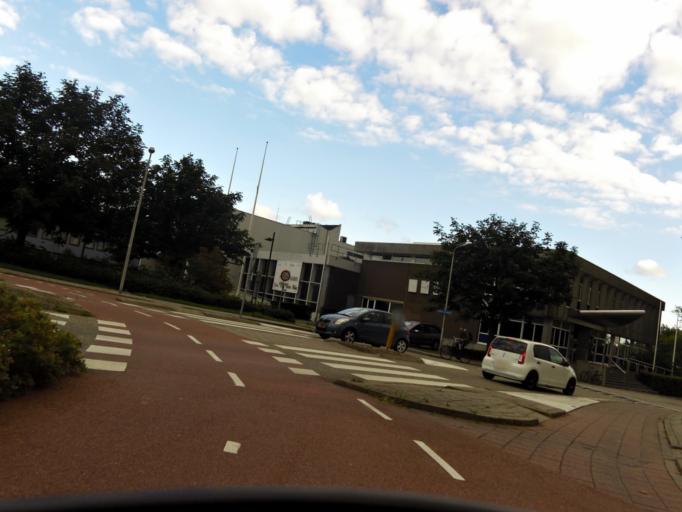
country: NL
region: South Holland
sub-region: Gemeente Leiderdorp
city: Leiderdorp
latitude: 52.1291
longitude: 4.5878
